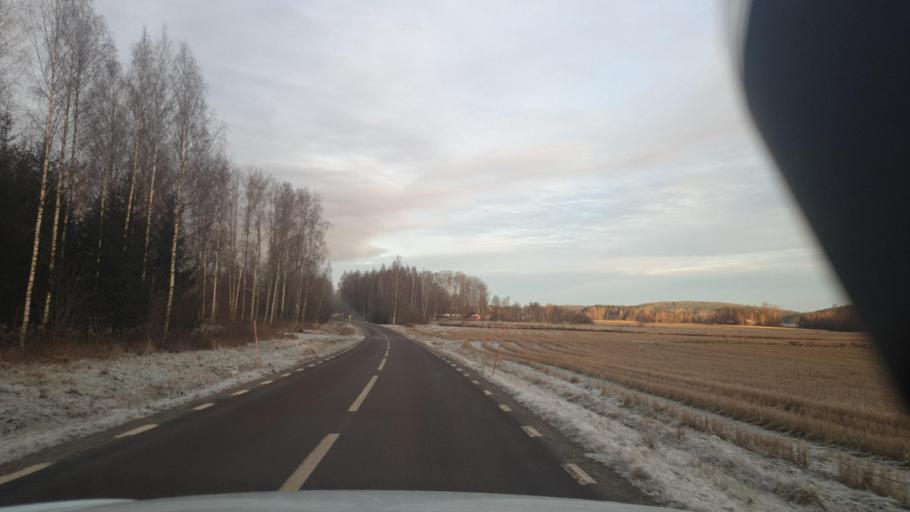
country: SE
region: Vaermland
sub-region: Arvika Kommun
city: Arvika
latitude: 59.6019
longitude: 12.5354
